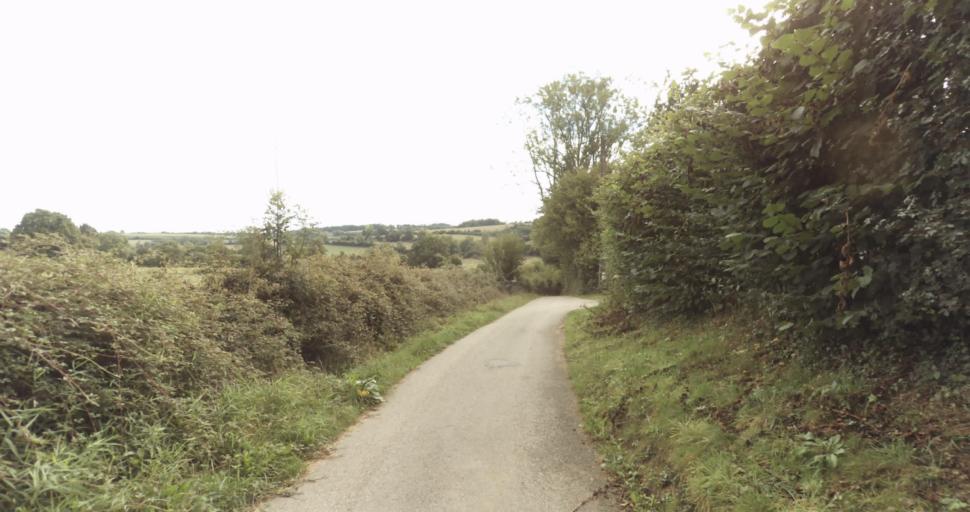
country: FR
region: Lower Normandy
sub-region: Departement de l'Orne
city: Gace
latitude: 48.8383
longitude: 0.2225
